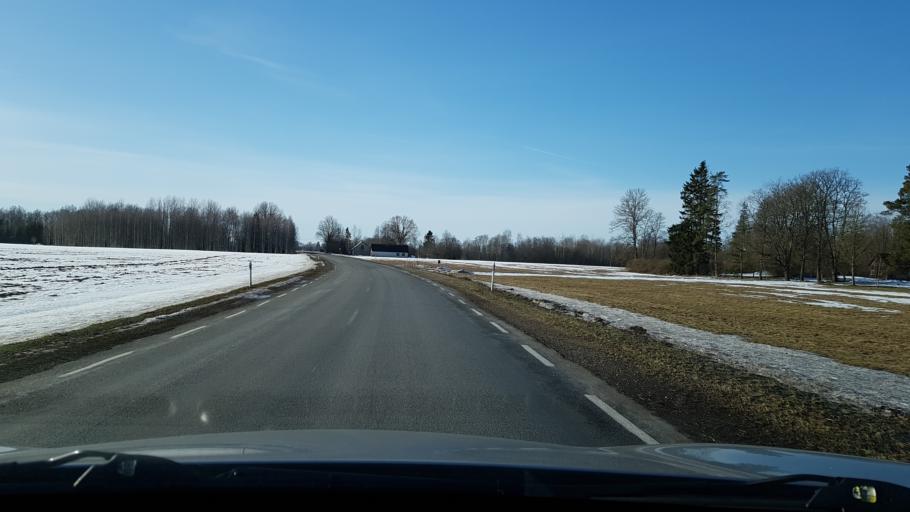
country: EE
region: Viljandimaa
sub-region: Vohma linn
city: Vohma
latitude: 58.6358
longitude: 25.6523
